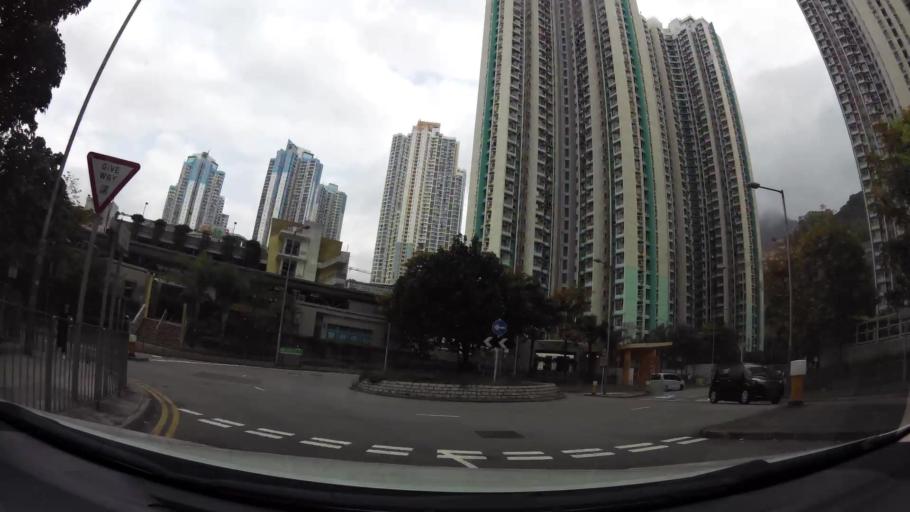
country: HK
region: Kowloon City
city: Kowloon
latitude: 22.3277
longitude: 114.2149
